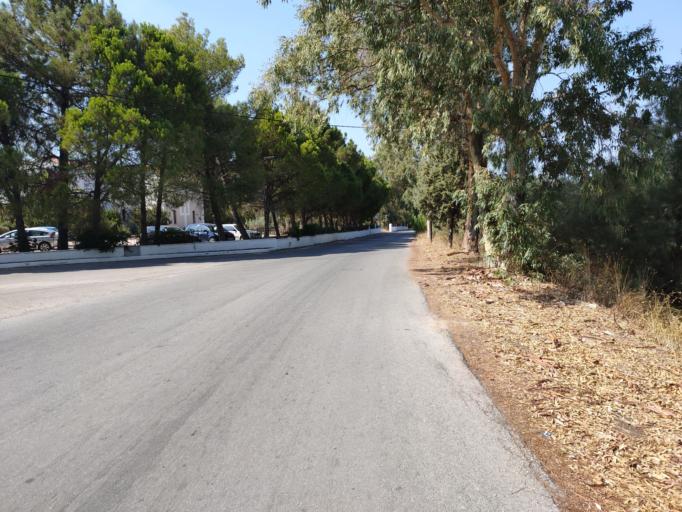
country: GR
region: North Aegean
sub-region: Nomos Lesvou
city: Kalloni
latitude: 39.2095
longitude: 26.2069
